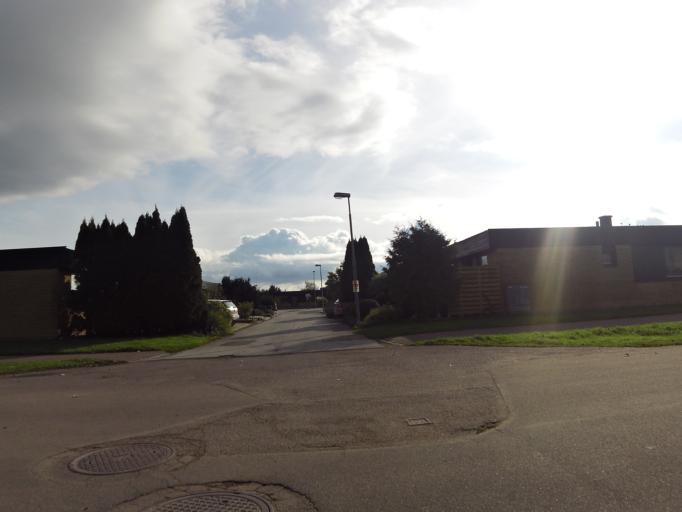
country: SE
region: Skane
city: Bjarred
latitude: 55.7165
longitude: 13.0368
